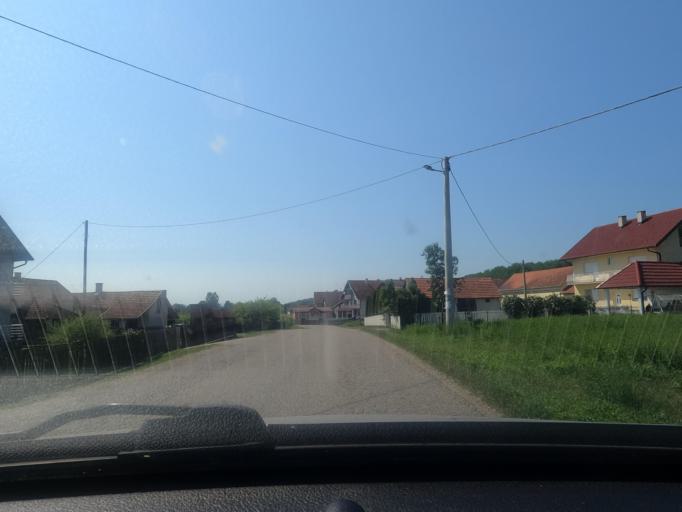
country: RS
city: Jadranska Lesnica
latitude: 44.5449
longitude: 19.3601
